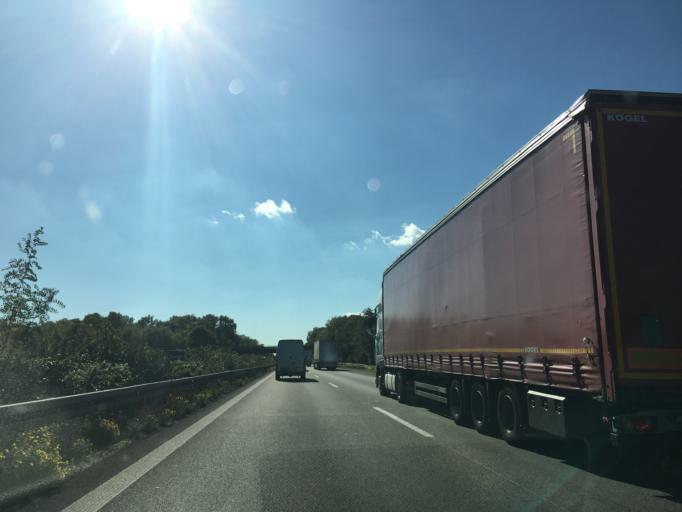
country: DE
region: Baden-Wuerttemberg
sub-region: Freiburg Region
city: Neuenburg am Rhein
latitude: 47.8161
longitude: 7.5544
